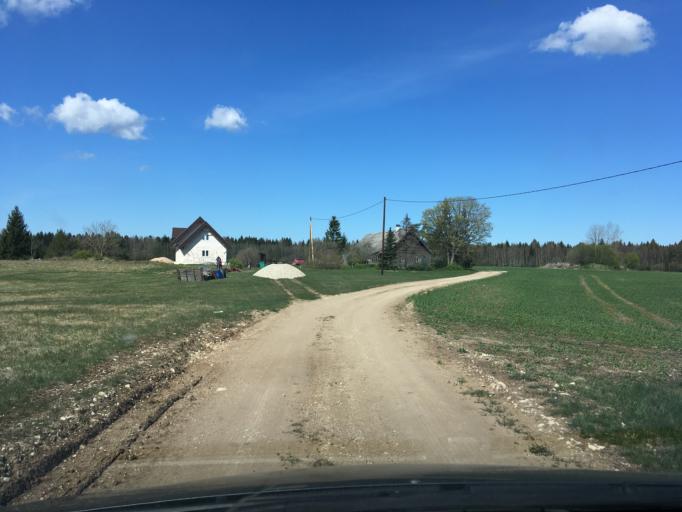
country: EE
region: Harju
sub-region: Raasiku vald
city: Raasiku
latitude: 59.2220
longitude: 25.1517
